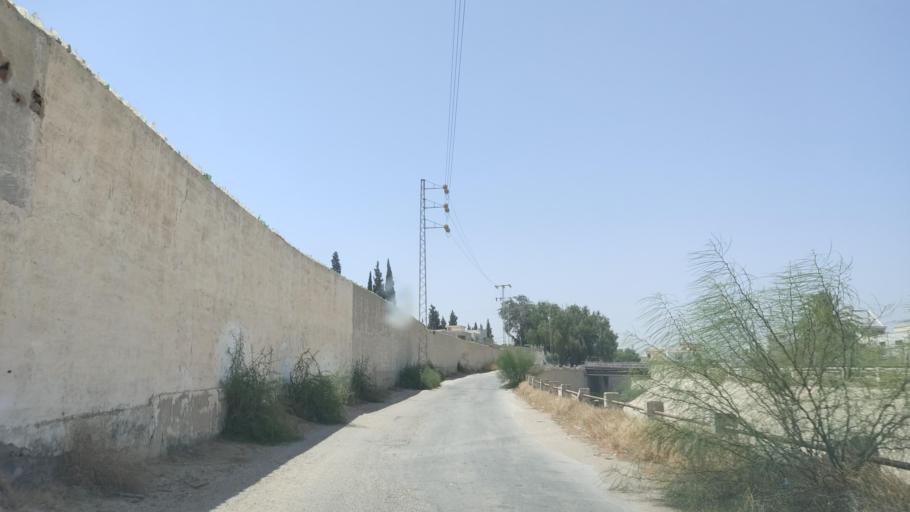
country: TN
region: Safaqis
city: Sfax
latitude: 34.7151
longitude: 10.7303
